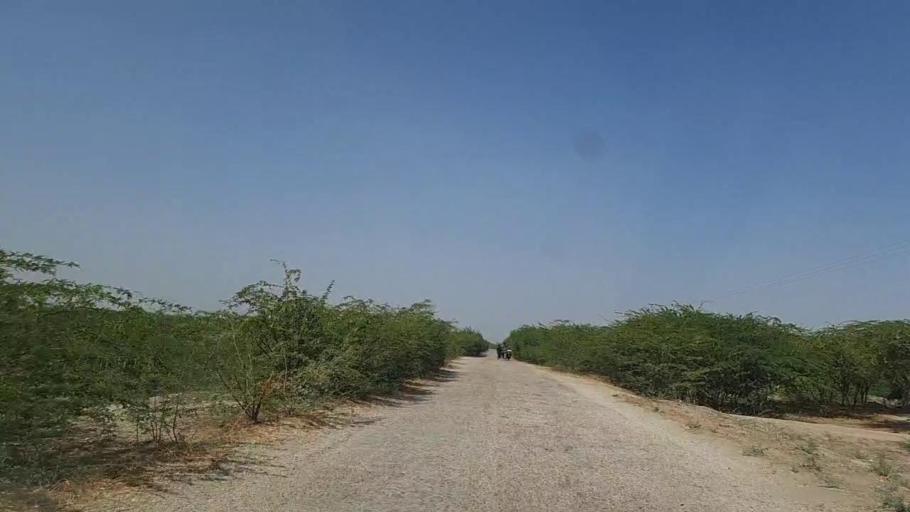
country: PK
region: Sindh
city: Naukot
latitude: 24.6468
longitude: 69.2879
